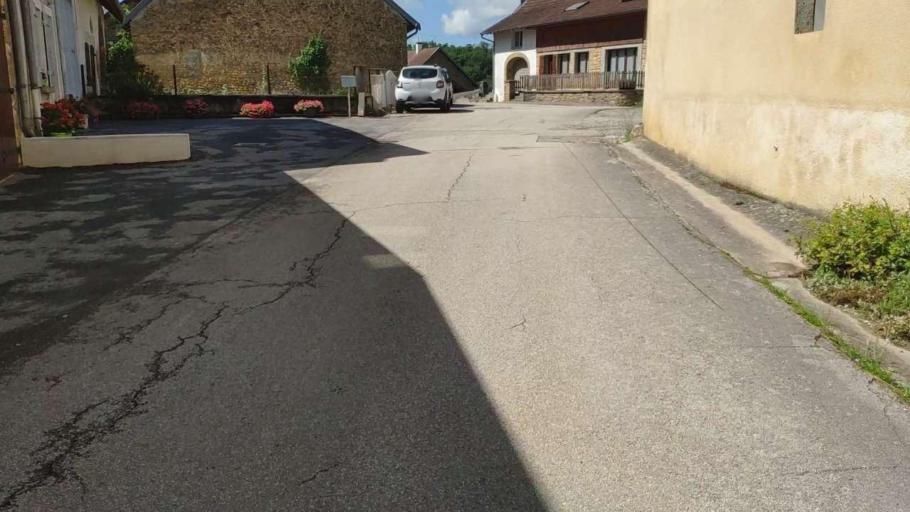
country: FR
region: Franche-Comte
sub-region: Departement du Jura
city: Bletterans
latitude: 46.8022
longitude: 5.5610
